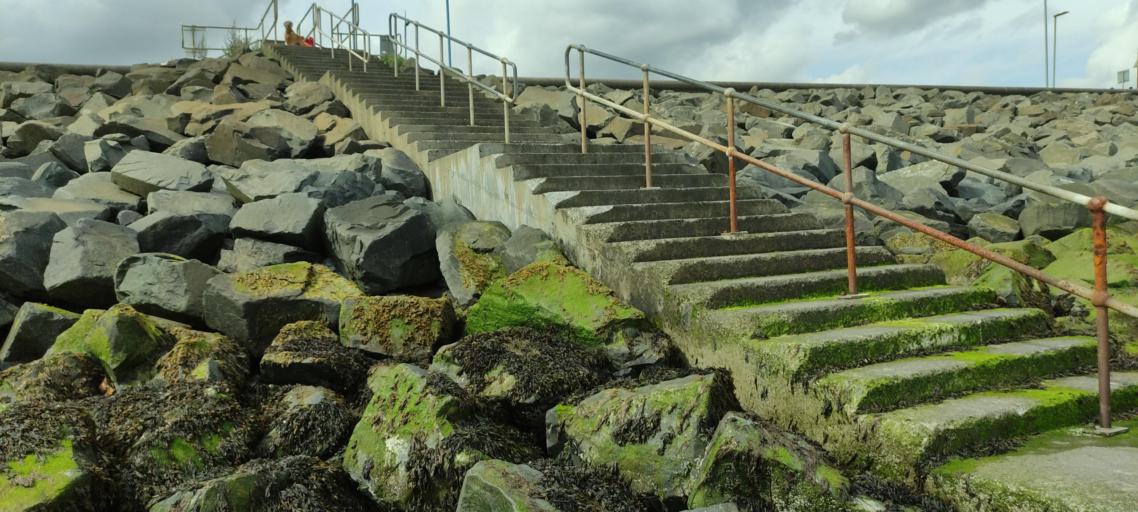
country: GB
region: England
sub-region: Hartlepool
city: Hartlepool
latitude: 54.6784
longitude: -1.1980
